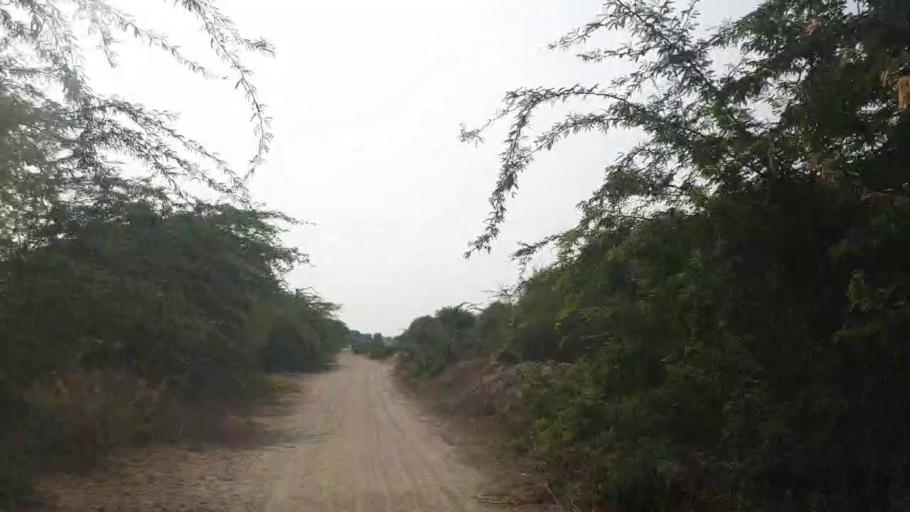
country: PK
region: Sindh
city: Badin
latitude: 24.6044
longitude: 68.7196
